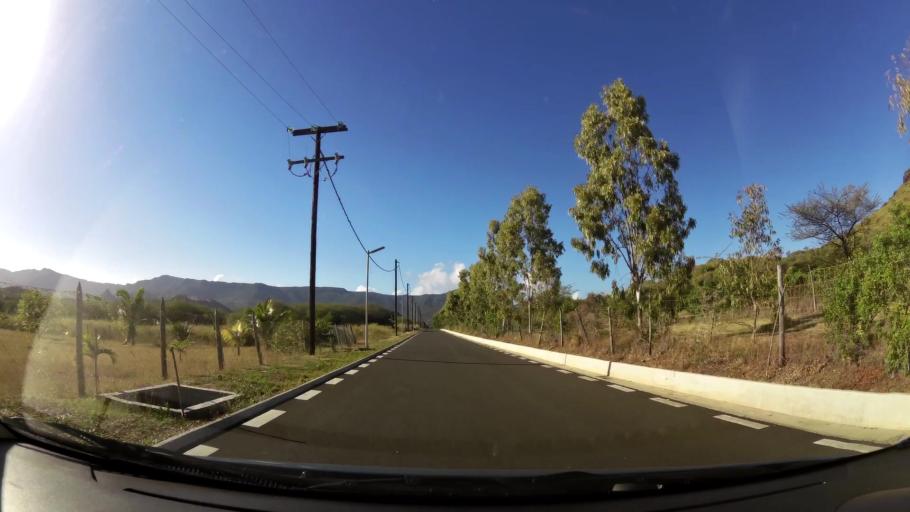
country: MU
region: Black River
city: Tamarin
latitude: -20.3389
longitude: 57.3853
